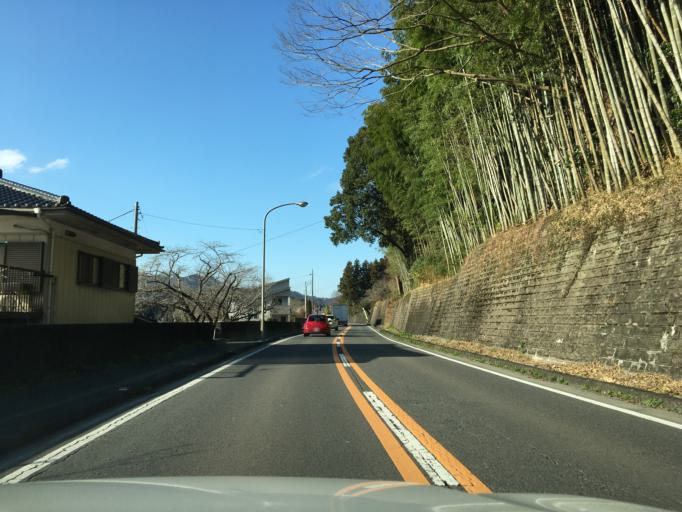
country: JP
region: Ibaraki
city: Daigo
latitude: 36.7004
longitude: 140.3838
